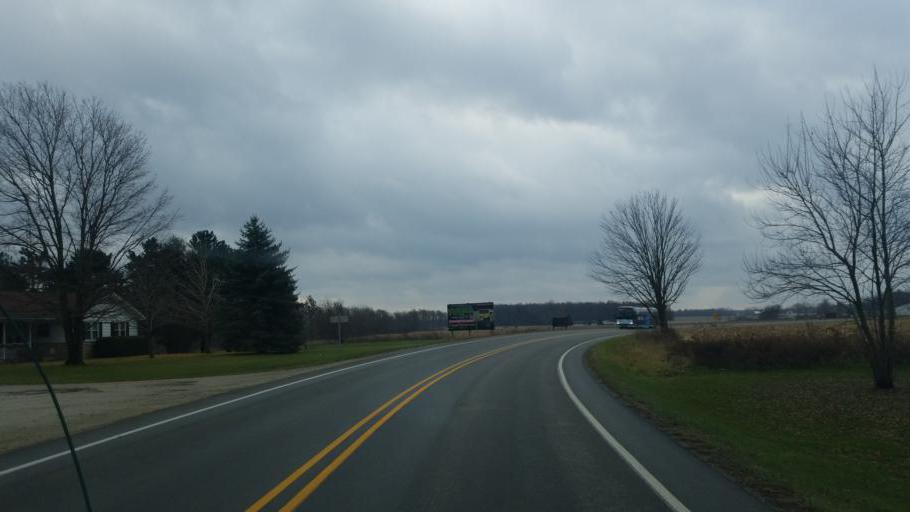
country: US
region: Indiana
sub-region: Adams County
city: Geneva
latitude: 40.5321
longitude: -84.9645
